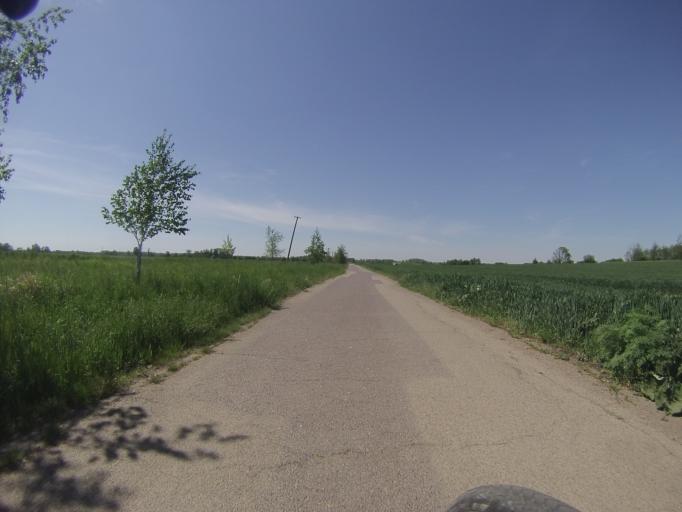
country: CZ
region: South Moravian
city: Novosedly
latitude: 48.8127
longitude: 16.4803
